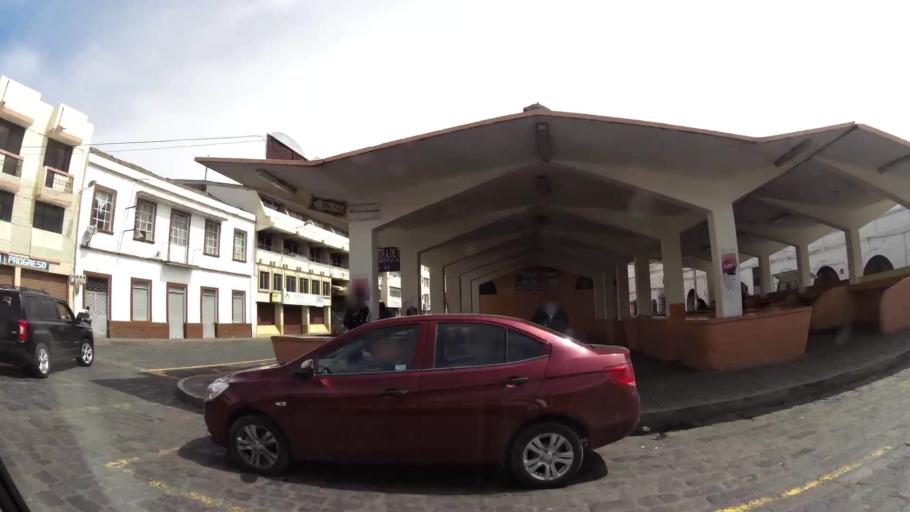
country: EC
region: Cotopaxi
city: Latacunga
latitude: -0.9297
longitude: -78.6147
